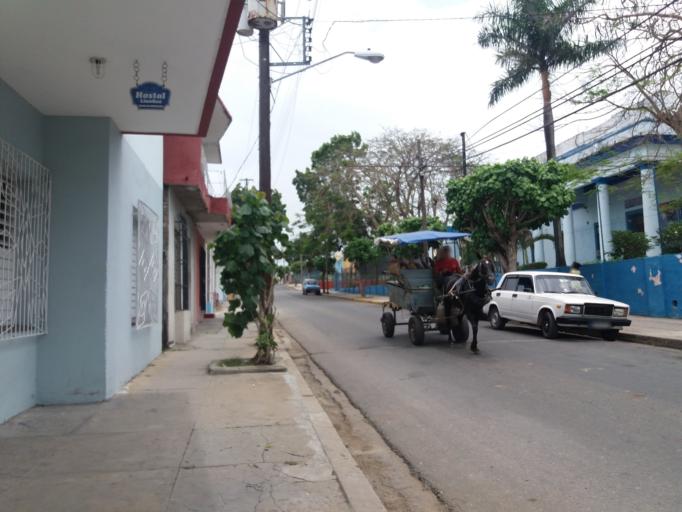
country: CU
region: Cienfuegos
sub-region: Municipio de Cienfuegos
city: Cienfuegos
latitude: 22.1474
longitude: -80.4450
